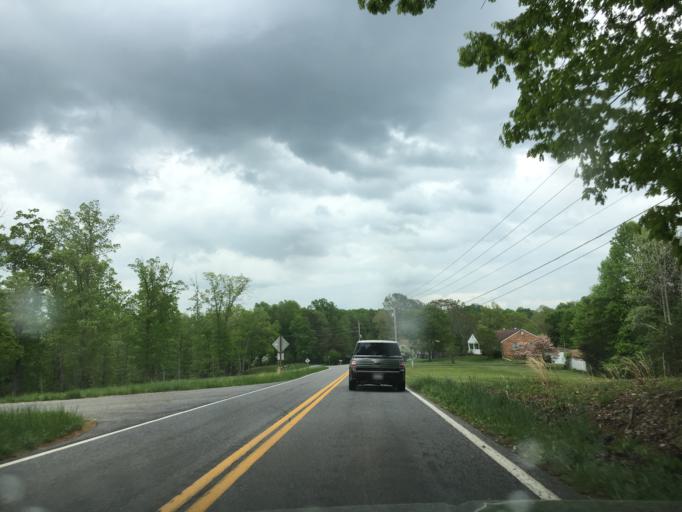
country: US
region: Virginia
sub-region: Campbell County
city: Rustburg
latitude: 37.3220
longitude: -79.1315
